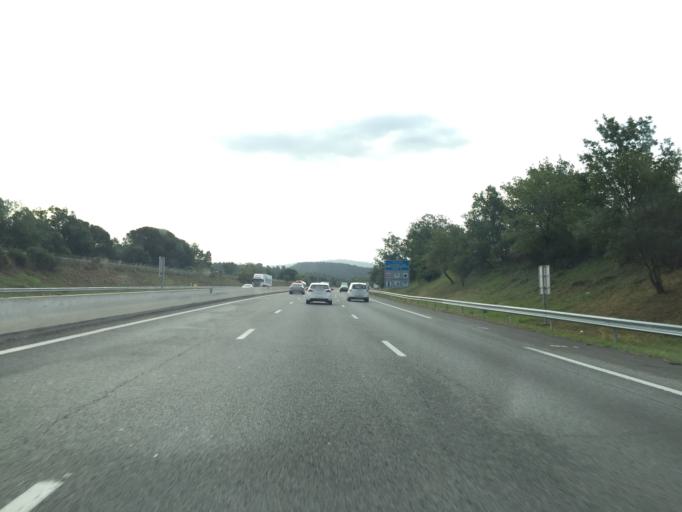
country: FR
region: Provence-Alpes-Cote d'Azur
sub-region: Departement du Var
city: Vidauban
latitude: 43.4145
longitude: 6.4357
